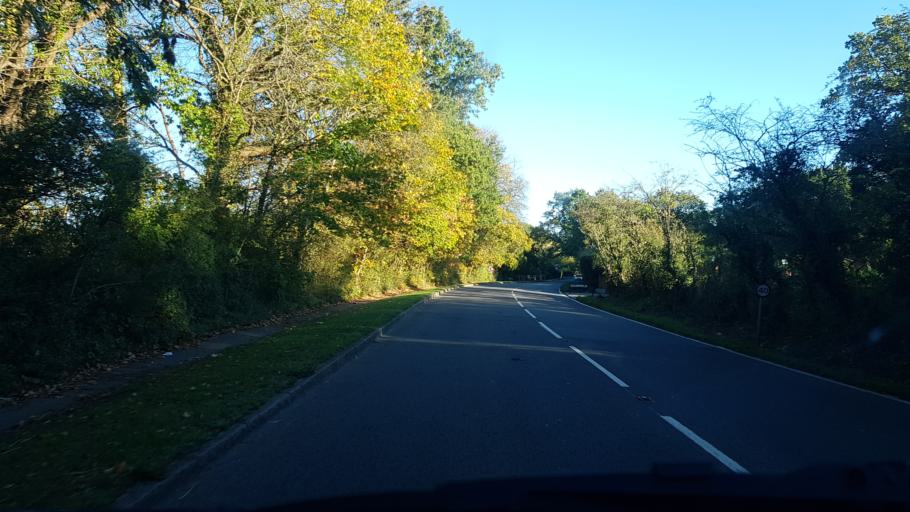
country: GB
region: England
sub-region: Surrey
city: Guildford
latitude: 51.2572
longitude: -0.6096
